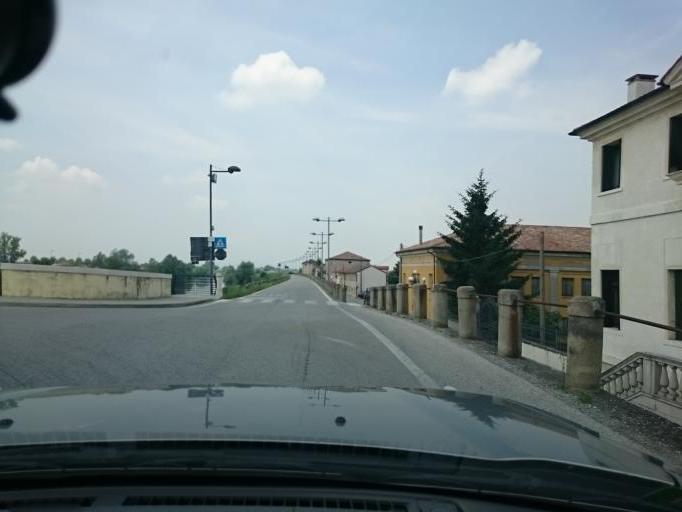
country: IT
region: Veneto
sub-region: Provincia di Padova
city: Pontelongo
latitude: 45.2502
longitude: 12.0193
